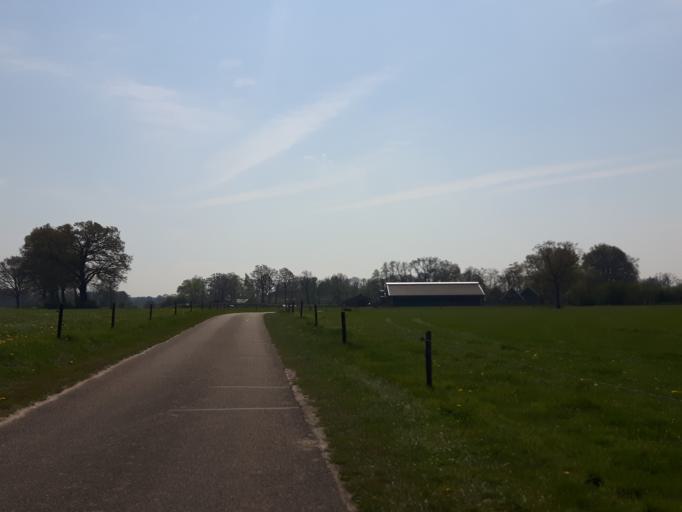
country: NL
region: Overijssel
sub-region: Gemeente Enschede
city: Enschede
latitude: 52.1421
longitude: 6.8381
